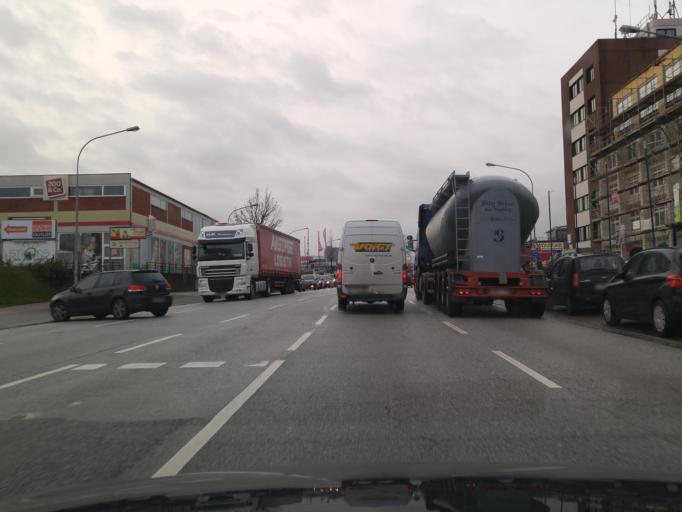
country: DE
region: Schleswig-Holstein
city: Luebeck
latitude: 53.8802
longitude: 10.6763
